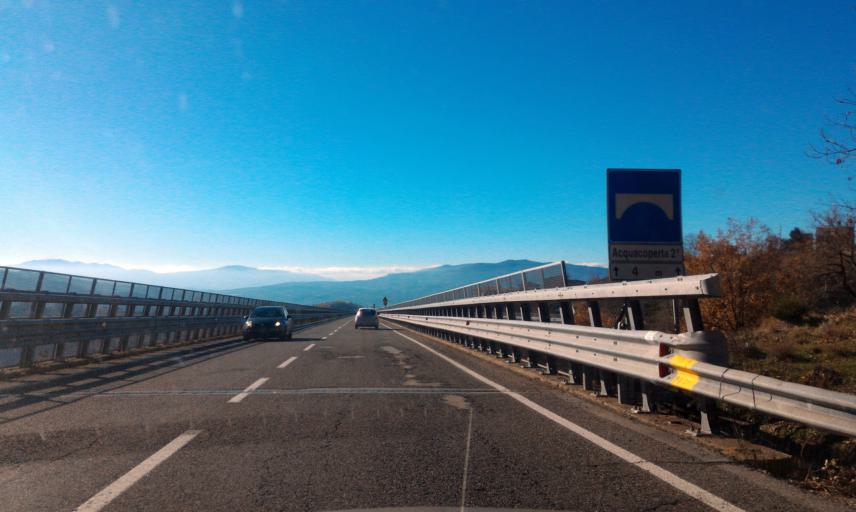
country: IT
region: Calabria
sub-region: Provincia di Cosenza
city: Spezzano Piccolo
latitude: 39.2926
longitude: 16.3507
